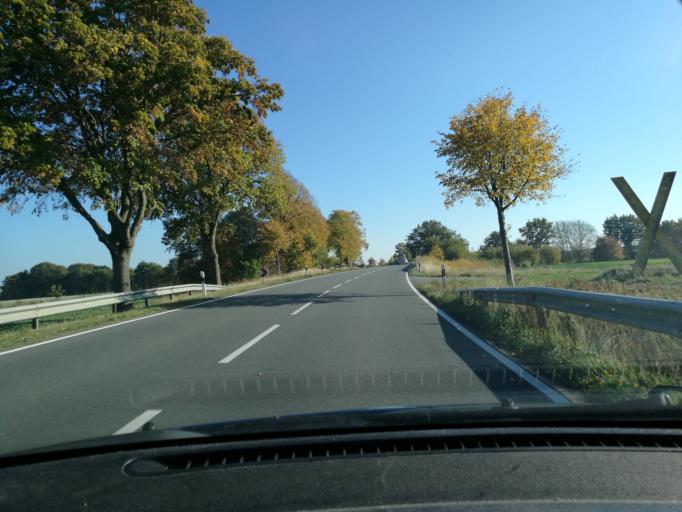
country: DE
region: Lower Saxony
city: Nahrendorf
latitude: 53.1633
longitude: 10.7970
